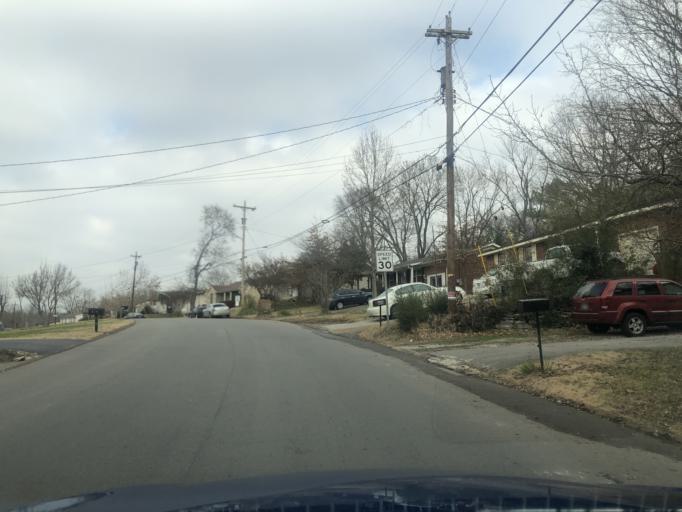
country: US
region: Tennessee
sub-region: Davidson County
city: Oak Hill
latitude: 36.0891
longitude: -86.7167
